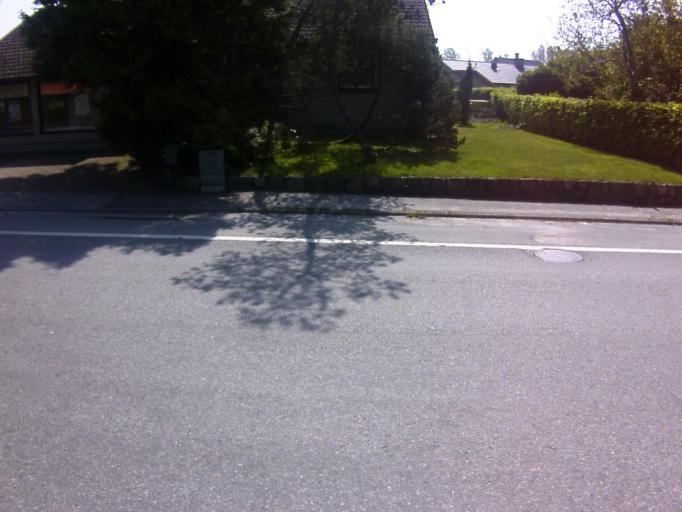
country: SE
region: Blekinge
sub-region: Solvesborgs Kommun
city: Soelvesborg
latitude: 56.0420
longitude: 14.5739
